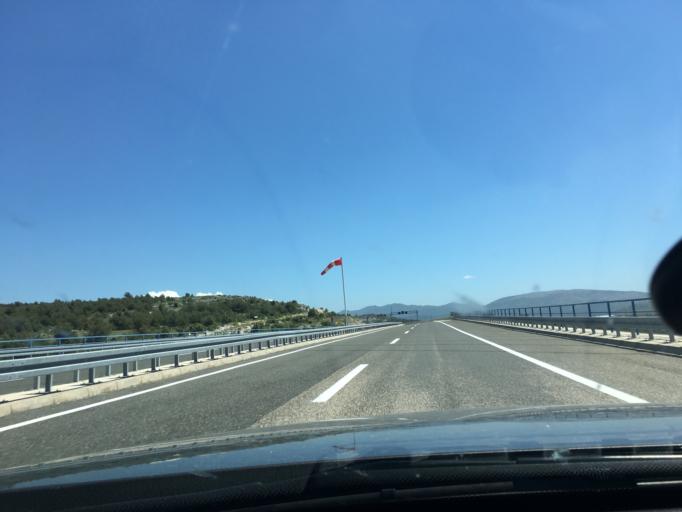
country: HR
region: Sibensko-Kniniska
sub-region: Grad Sibenik
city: Sibenik
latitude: 43.7284
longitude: 15.9772
